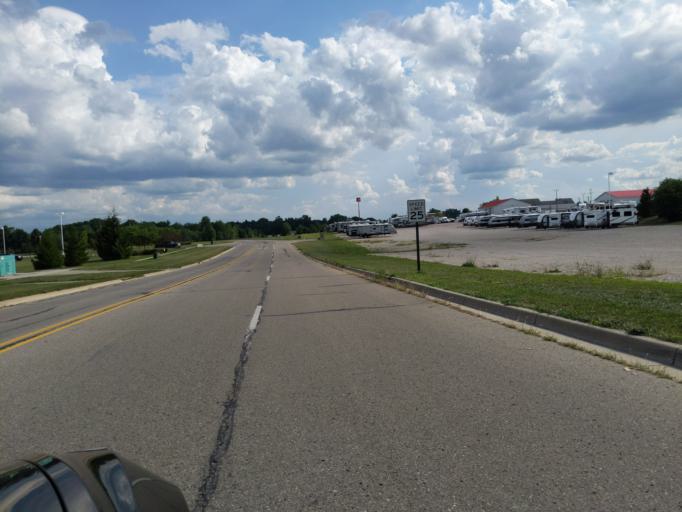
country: US
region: Michigan
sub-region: Clinton County
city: DeWitt
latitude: 42.8305
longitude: -84.5403
